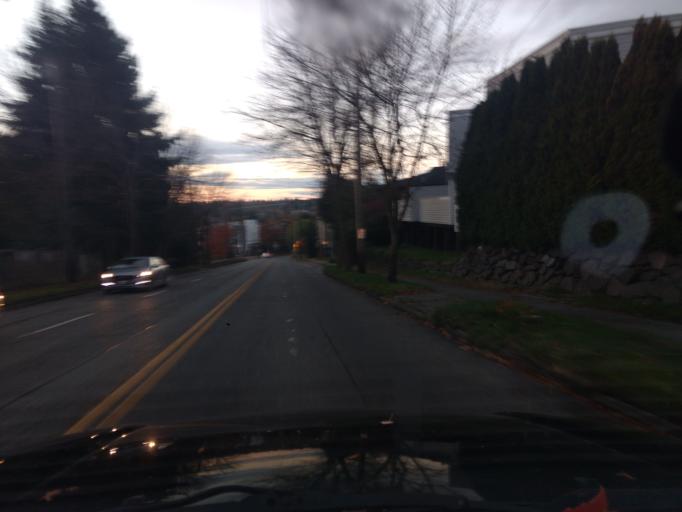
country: US
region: Washington
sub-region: King County
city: Seattle
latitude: 47.6673
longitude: -122.3611
